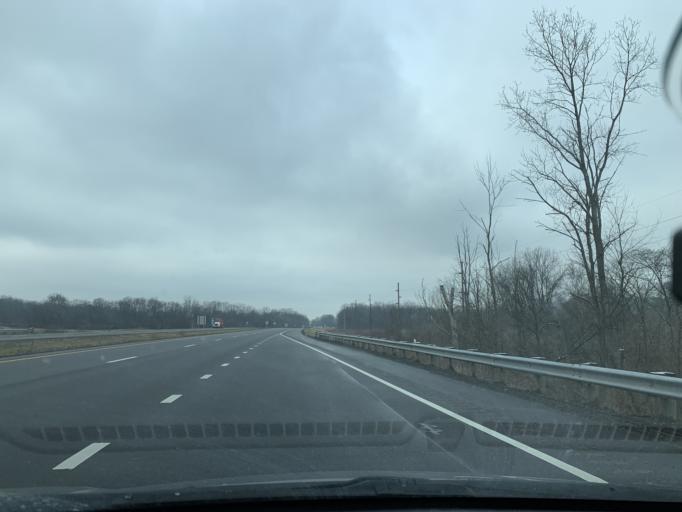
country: US
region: Ohio
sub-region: Licking County
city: Granville South
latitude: 40.0628
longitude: -82.5343
